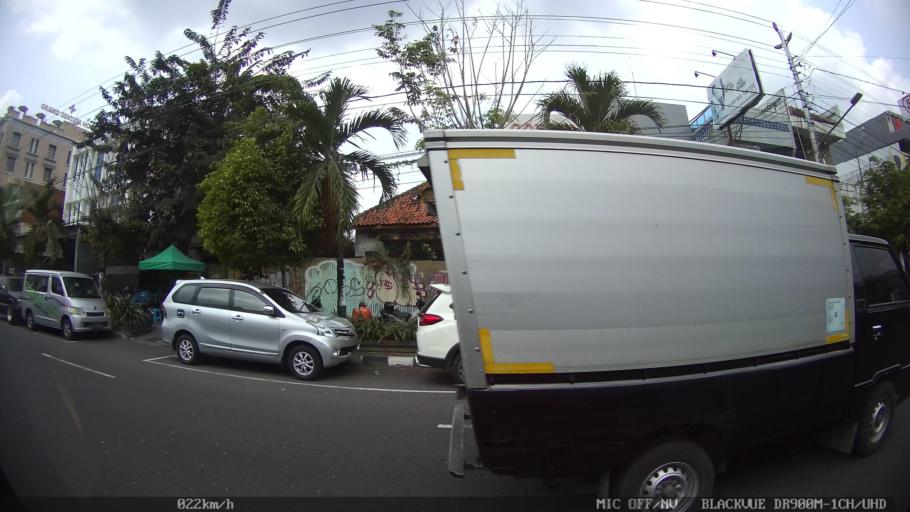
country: ID
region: Daerah Istimewa Yogyakarta
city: Yogyakarta
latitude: -7.7840
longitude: 110.3647
